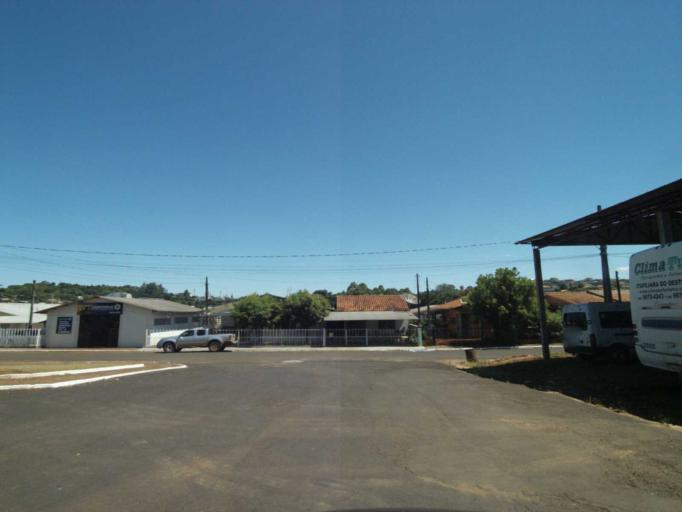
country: BR
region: Parana
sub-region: Coronel Vivida
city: Coronel Vivida
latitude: -25.9655
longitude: -52.8166
